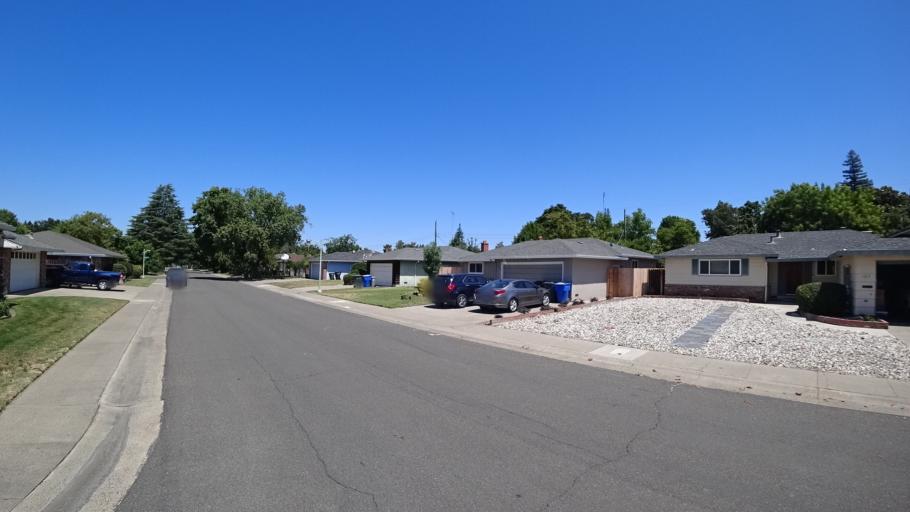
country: US
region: California
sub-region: Yolo County
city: West Sacramento
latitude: 38.5310
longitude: -121.5137
